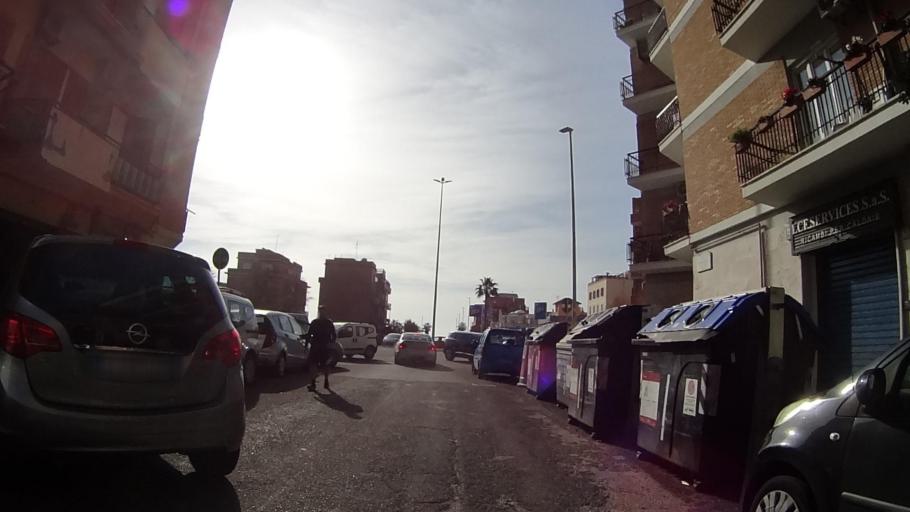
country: IT
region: Latium
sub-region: Citta metropolitana di Roma Capitale
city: Lido di Ostia
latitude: 41.7361
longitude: 12.2670
